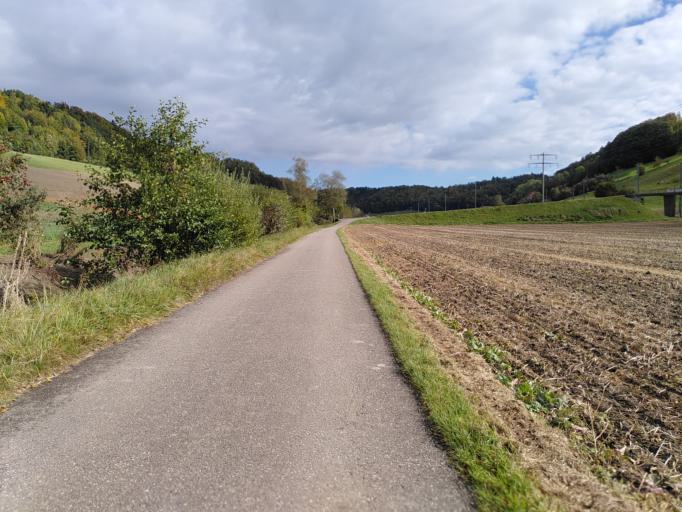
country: CH
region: Bern
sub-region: Oberaargau
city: Seeberg
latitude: 47.1338
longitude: 7.6825
